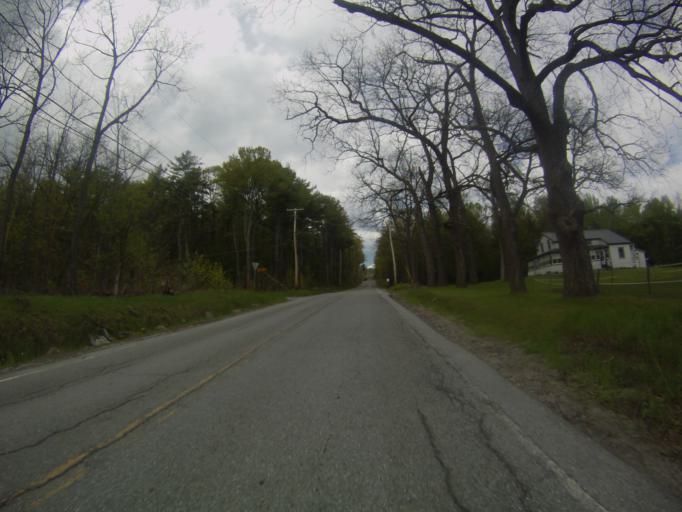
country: US
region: New York
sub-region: Essex County
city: Mineville
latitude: 44.0770
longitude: -73.5275
